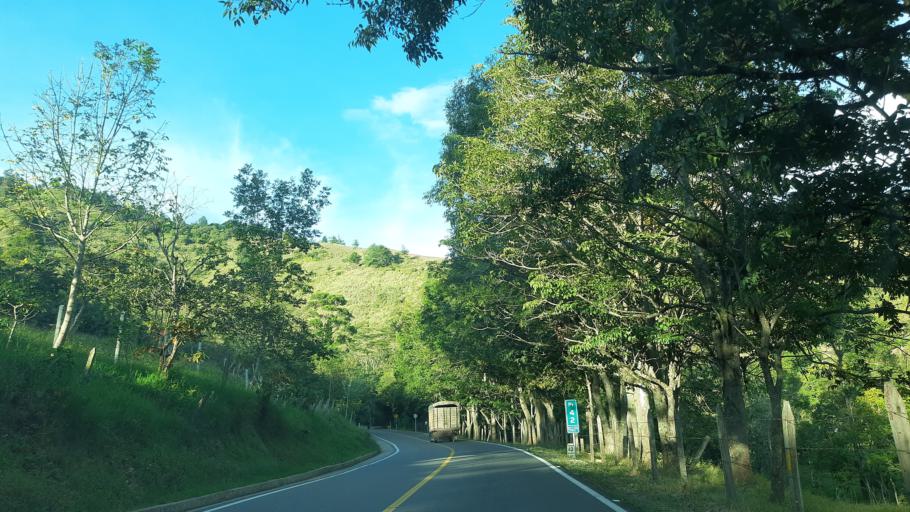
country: CO
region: Boyaca
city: Guateque
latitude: 5.0055
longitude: -73.4999
